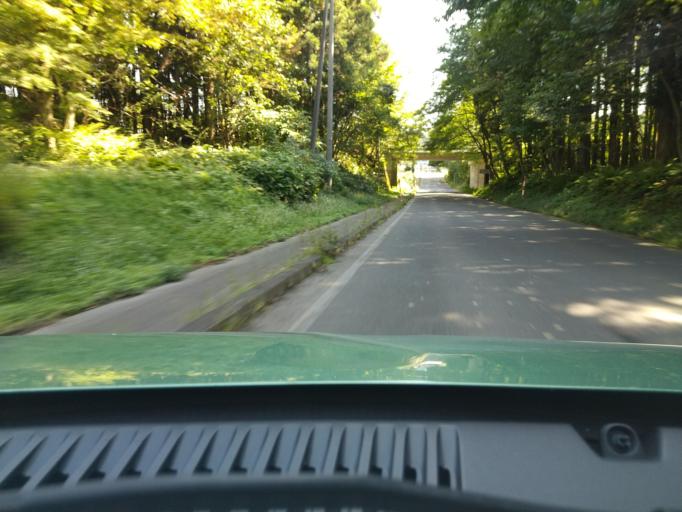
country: JP
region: Akita
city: Omagari
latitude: 39.6031
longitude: 140.3255
